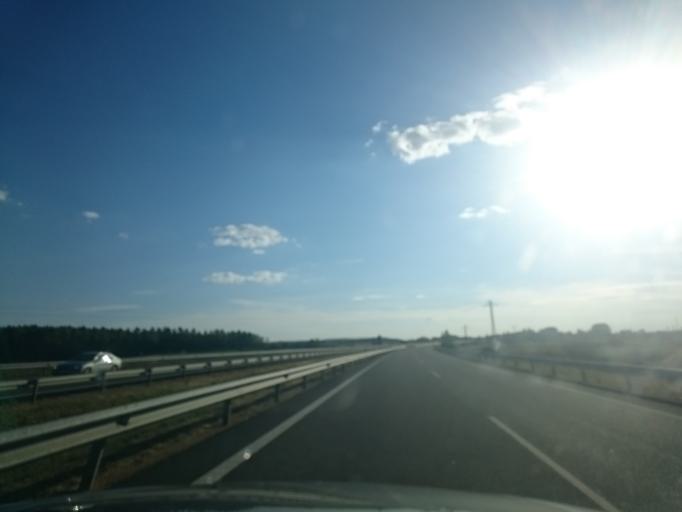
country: ES
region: Castille and Leon
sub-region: Provincia de Burgos
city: Melgar de Fernamental
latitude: 42.4093
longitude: -4.2673
